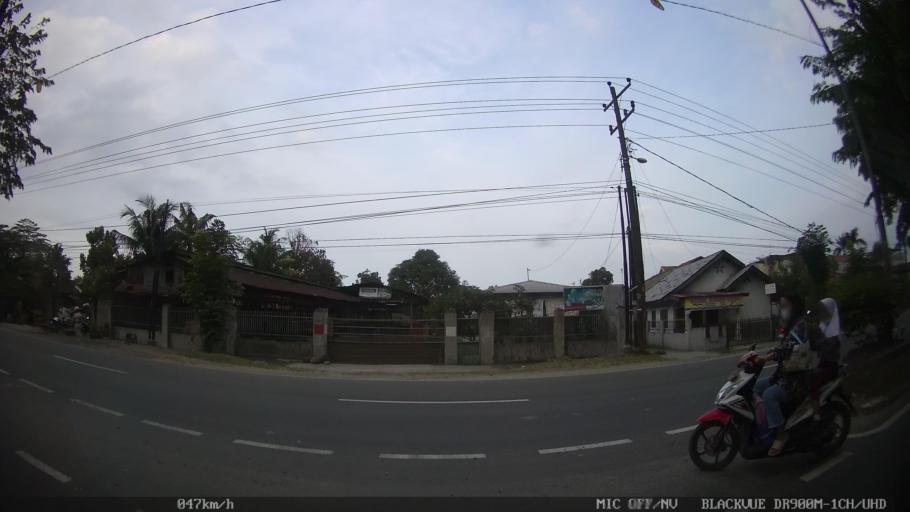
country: ID
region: North Sumatra
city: Sunggal
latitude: 3.5647
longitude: 98.6156
